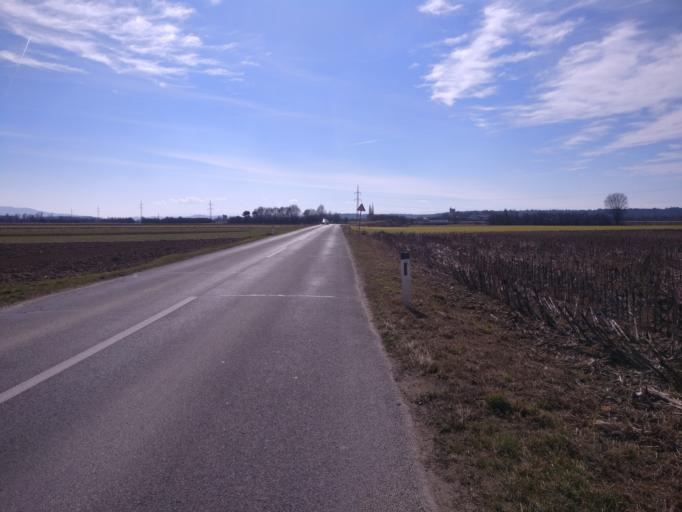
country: AT
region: Styria
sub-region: Politischer Bezirk Graz-Umgebung
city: Zettling
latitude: 46.9578
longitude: 15.4452
